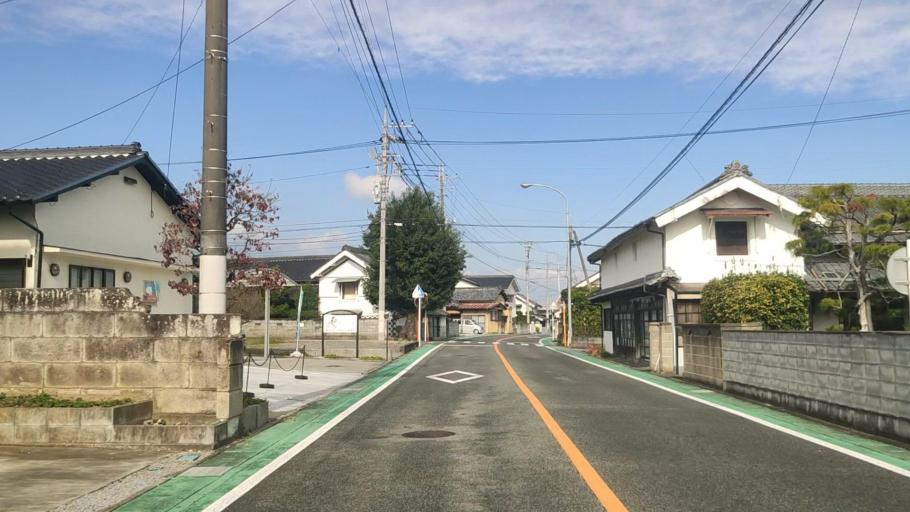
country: JP
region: Yamanashi
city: Ryuo
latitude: 35.5651
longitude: 138.4650
